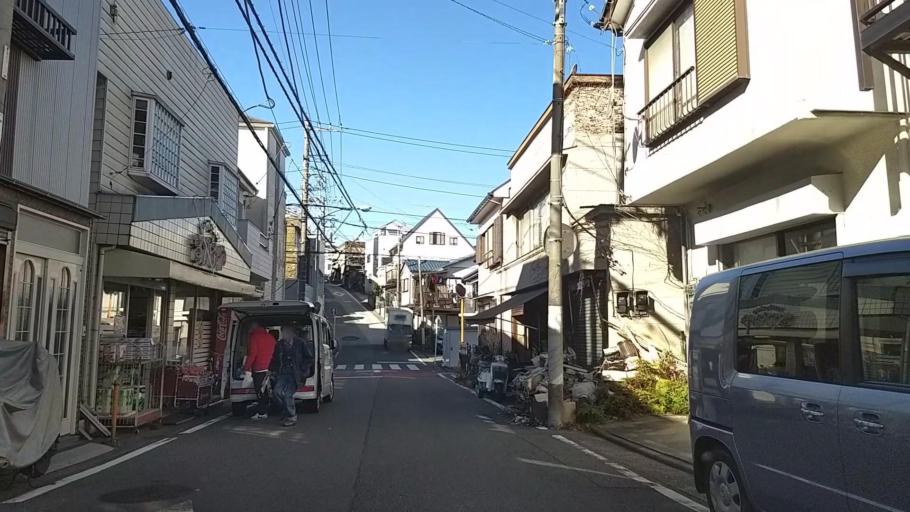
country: JP
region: Kanagawa
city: Yokohama
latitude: 35.4493
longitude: 139.6181
